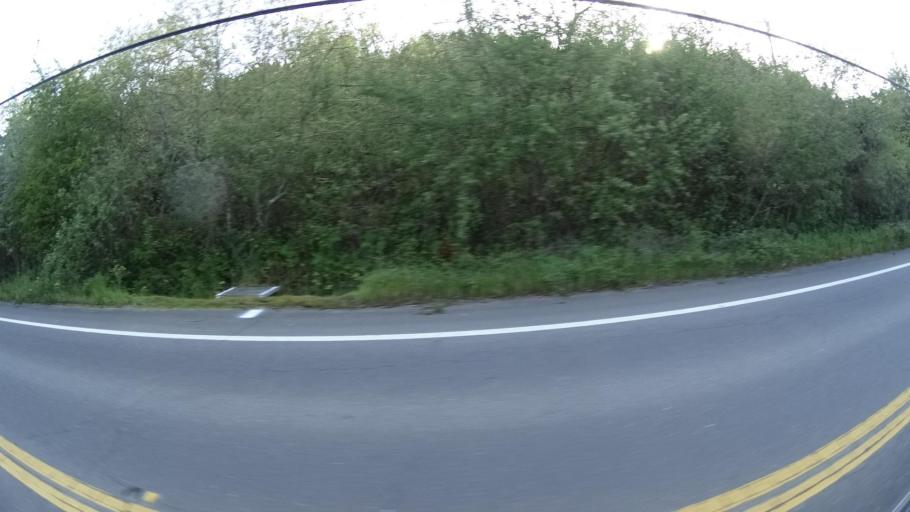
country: US
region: California
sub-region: Humboldt County
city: Myrtletown
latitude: 40.7682
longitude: -124.0690
